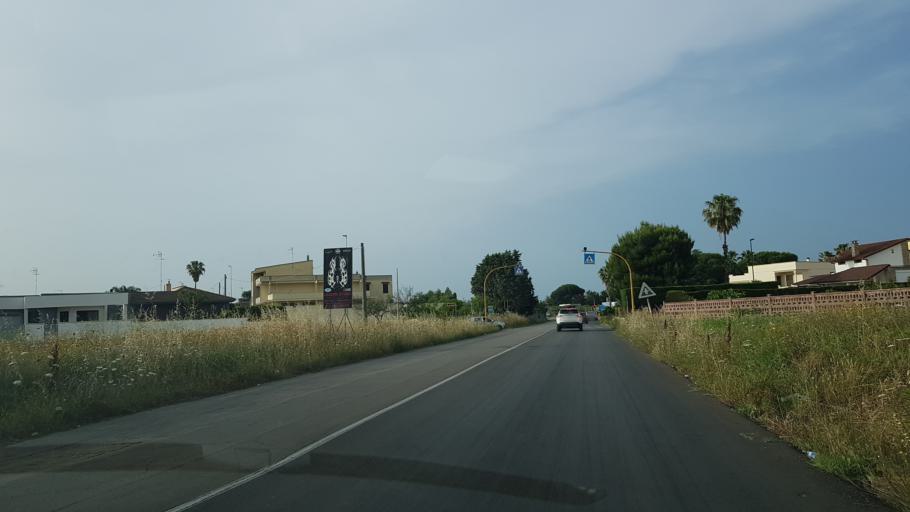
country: IT
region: Apulia
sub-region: Provincia di Brindisi
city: San Pietro Vernotico
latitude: 40.4966
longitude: 17.9922
